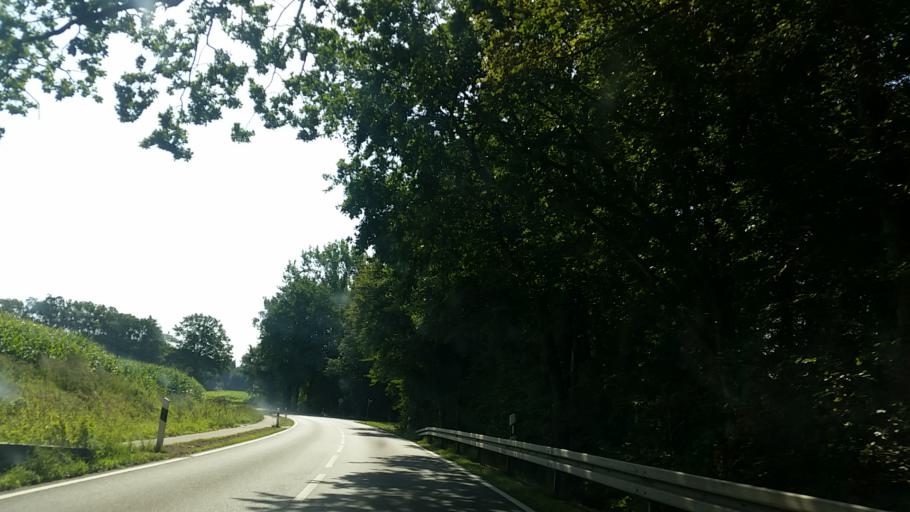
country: DE
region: Lower Saxony
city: Ankum
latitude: 52.5287
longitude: 7.8937
